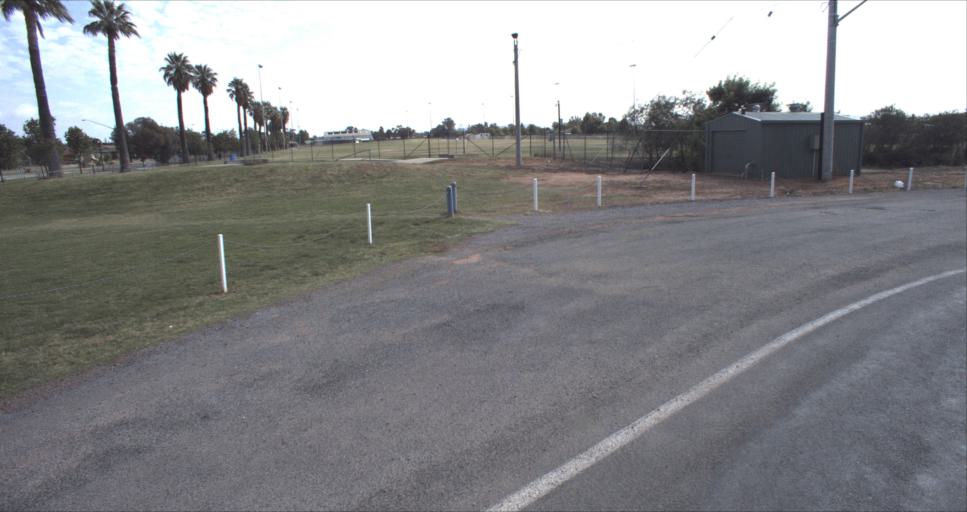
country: AU
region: New South Wales
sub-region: Leeton
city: Leeton
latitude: -34.5564
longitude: 146.4116
